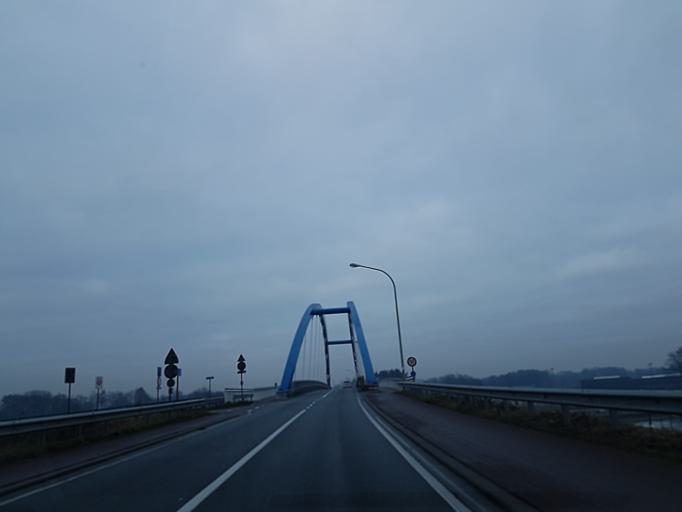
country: BE
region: Flanders
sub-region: Provincie Antwerpen
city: Grobbendonk
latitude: 51.1789
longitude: 4.7447
